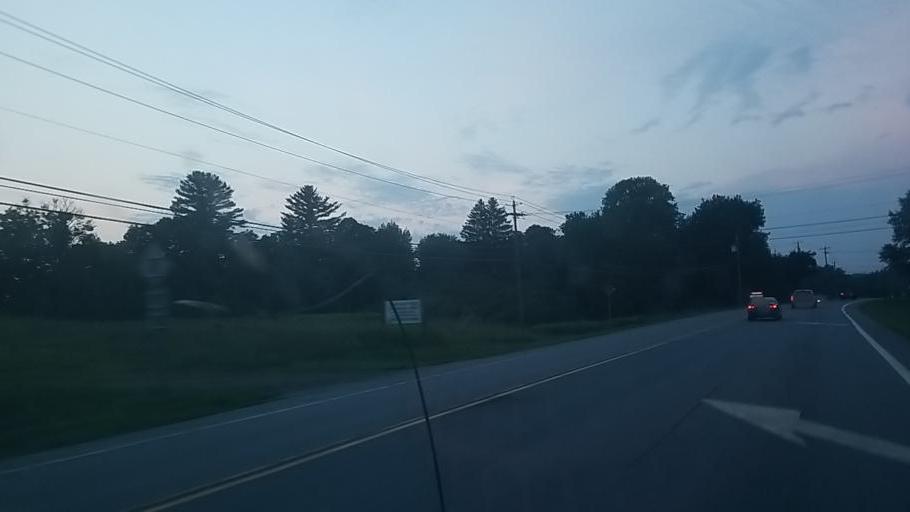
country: US
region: New York
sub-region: Montgomery County
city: Fonda
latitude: 42.9601
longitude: -74.3862
